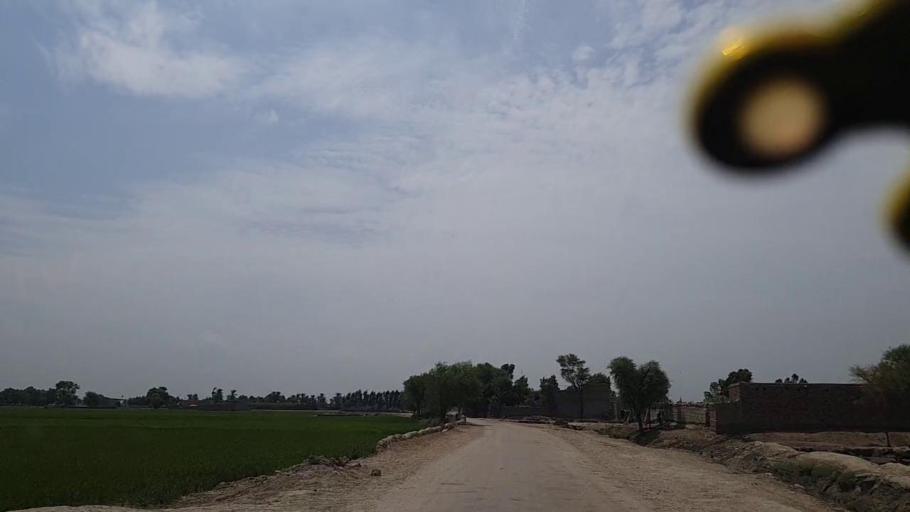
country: PK
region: Sindh
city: Thul
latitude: 28.1144
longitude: 68.8602
